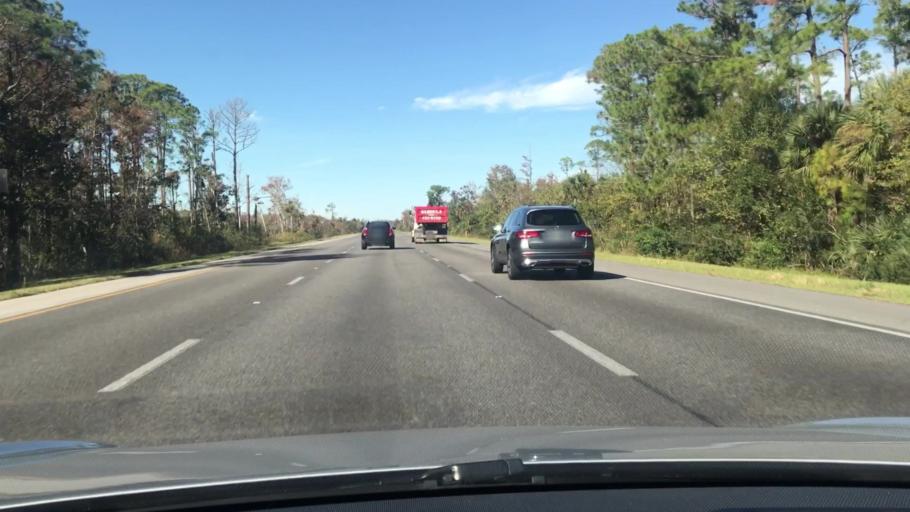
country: US
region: Florida
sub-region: Volusia County
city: Glencoe
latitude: 29.0225
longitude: -80.9940
